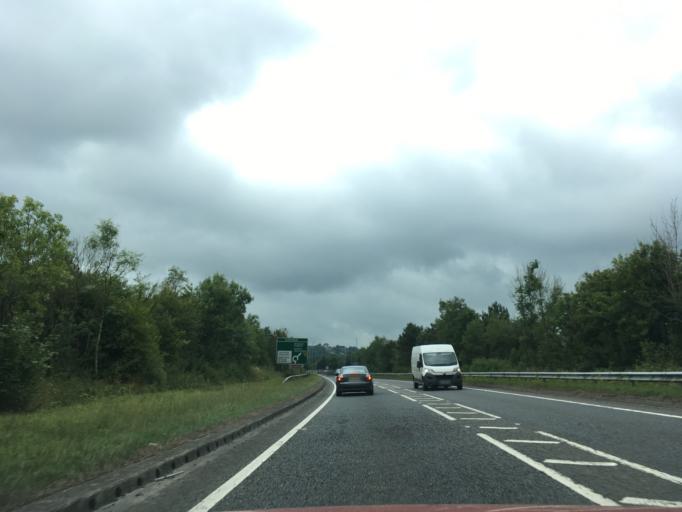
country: GB
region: Wales
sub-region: Carmarthenshire
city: Whitland
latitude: 51.8232
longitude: -4.6233
